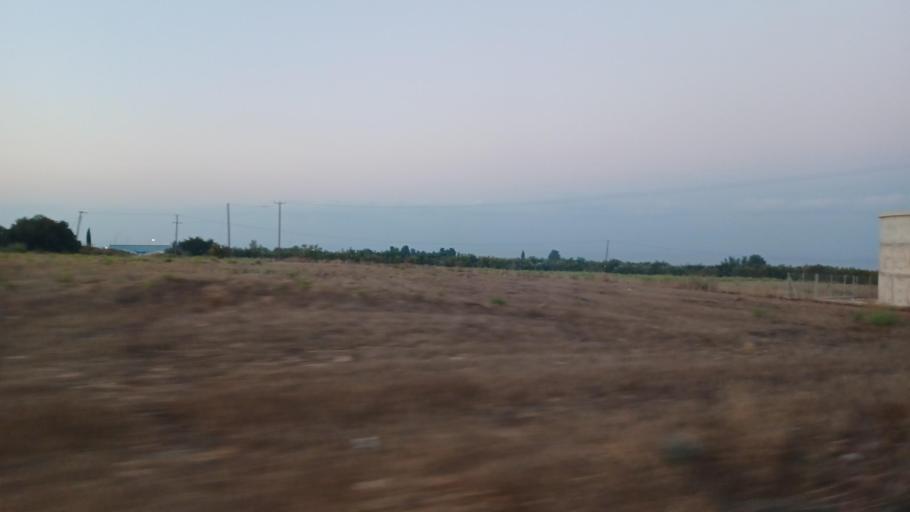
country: CY
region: Pafos
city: Empa
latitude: 34.8107
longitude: 32.4399
